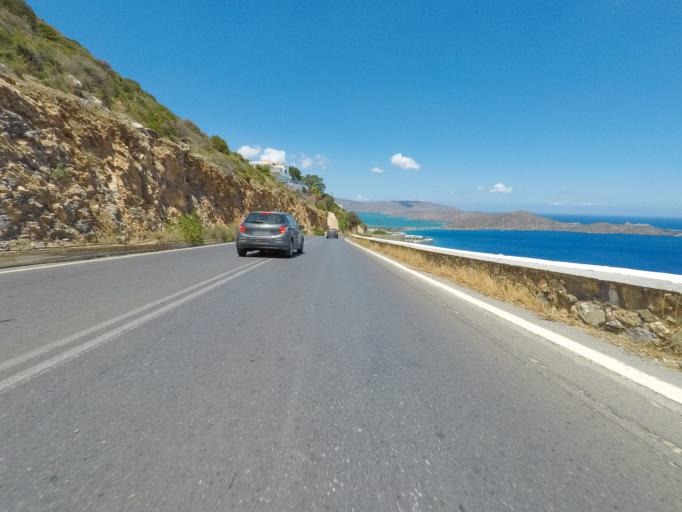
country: GR
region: Crete
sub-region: Nomos Lasithiou
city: Skhisma
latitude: 35.2344
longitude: 25.7282
